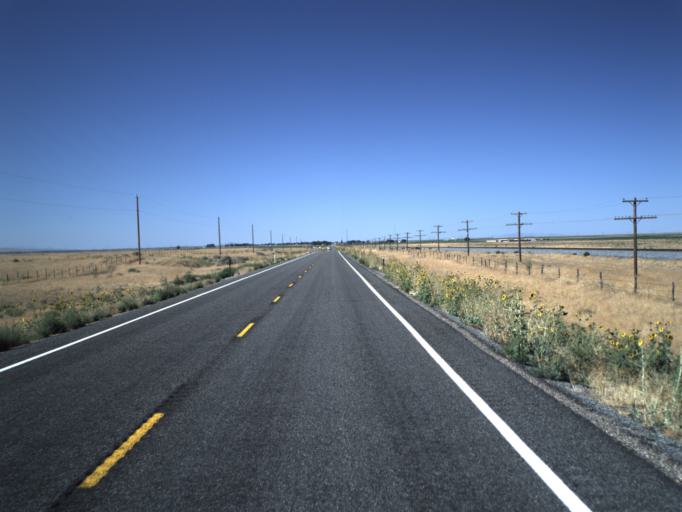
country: US
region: Utah
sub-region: Millard County
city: Delta
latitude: 39.5784
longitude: -112.3383
